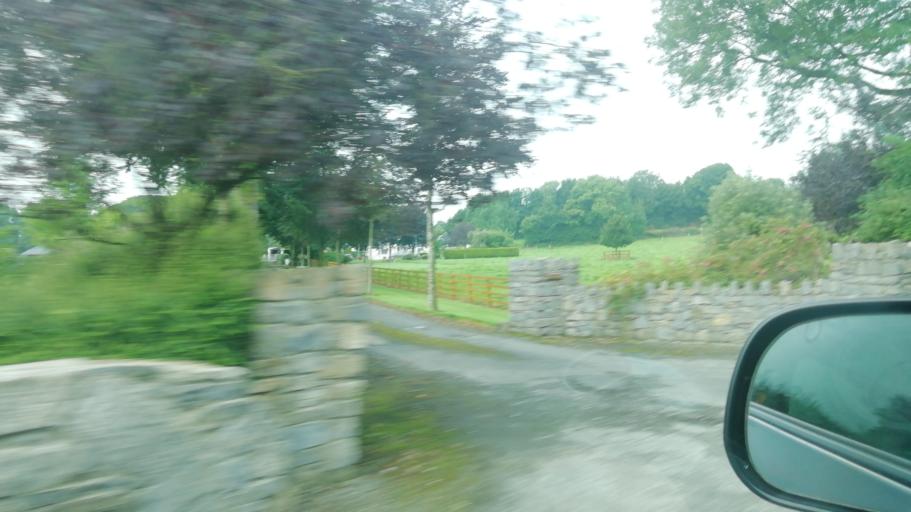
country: IE
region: Munster
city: Fethard
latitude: 52.5691
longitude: -7.5811
